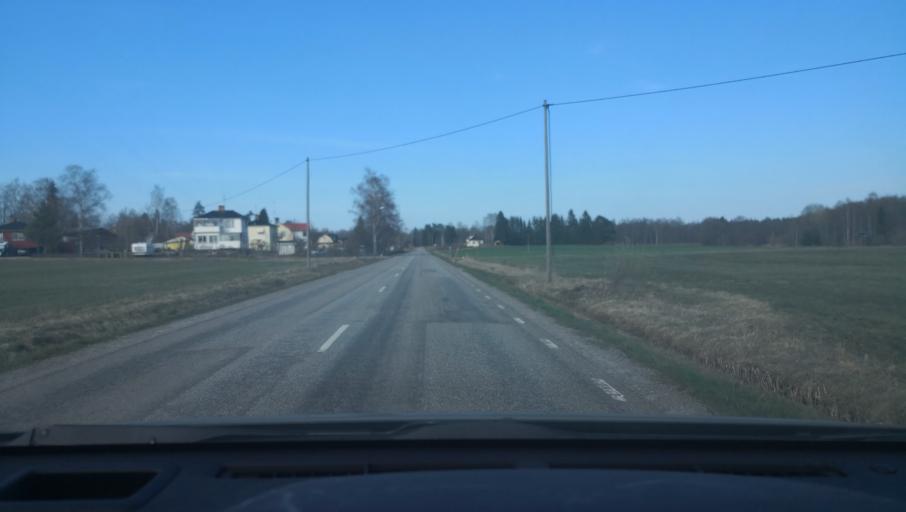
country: SE
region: Uppsala
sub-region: Heby Kommun
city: Heby
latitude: 59.9537
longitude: 16.8762
